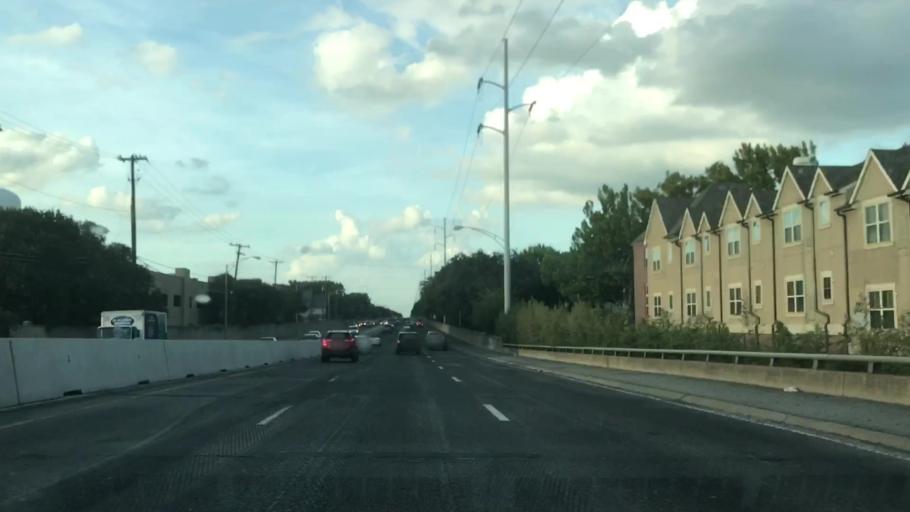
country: US
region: Texas
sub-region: Dallas County
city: Highland Park
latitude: 32.8217
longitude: -96.8168
